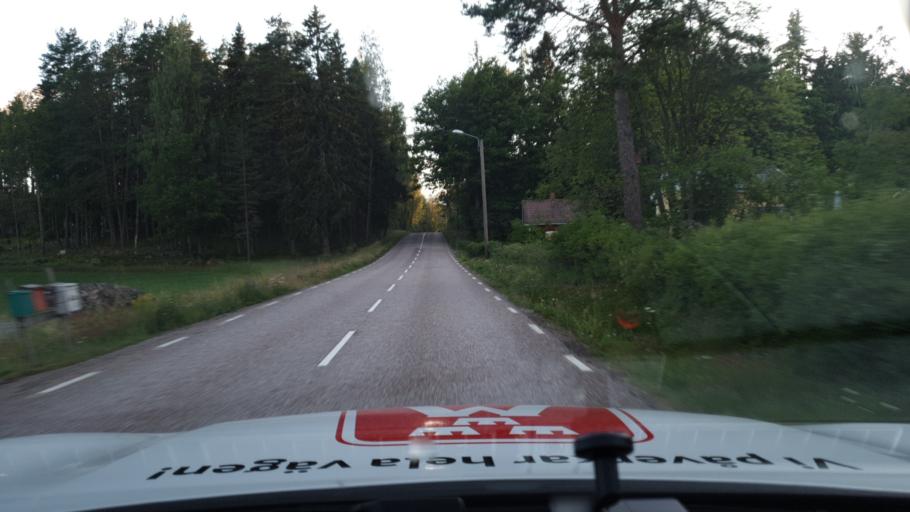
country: SE
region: Dalarna
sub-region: Avesta Kommun
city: Horndal
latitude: 60.1701
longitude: 16.4900
